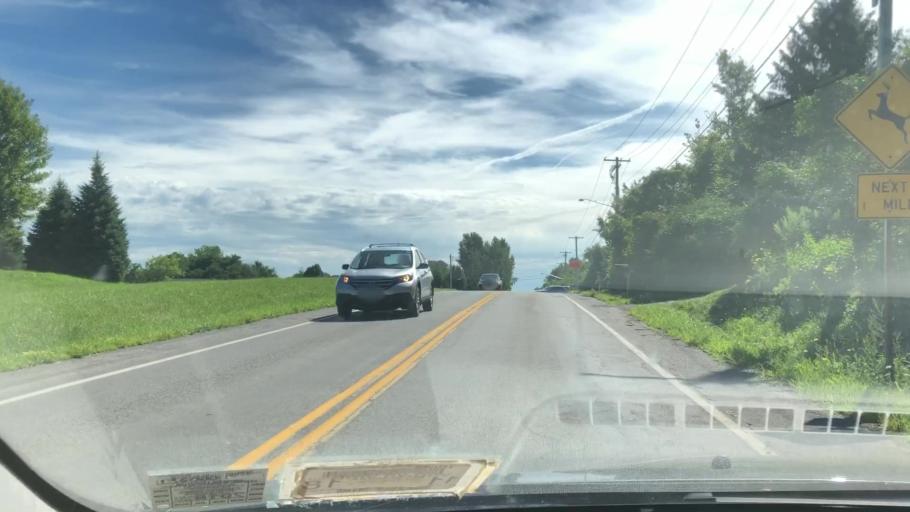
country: US
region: New York
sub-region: Monroe County
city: Fairport
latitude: 43.1086
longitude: -77.3957
